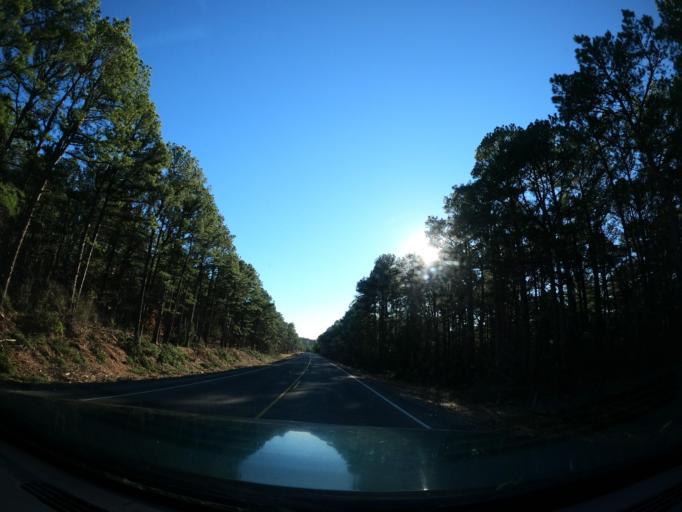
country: US
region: Oklahoma
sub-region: Latimer County
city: Wilburton
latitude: 34.9913
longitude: -95.3510
